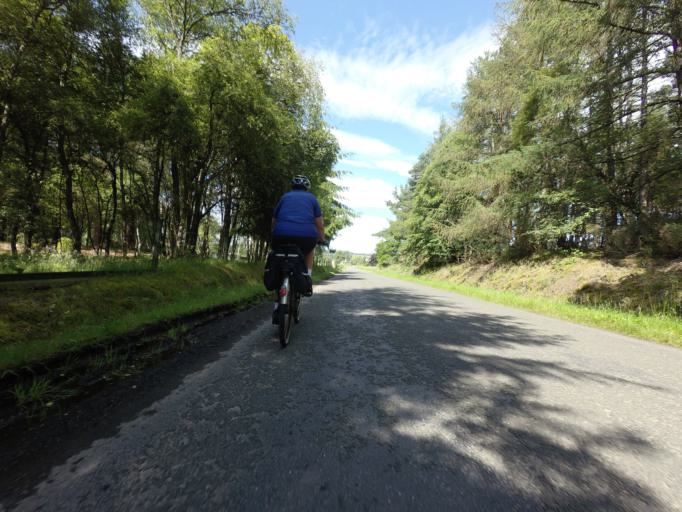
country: GB
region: Scotland
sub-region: Highland
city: Conon Bridge
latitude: 57.5383
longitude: -4.3280
